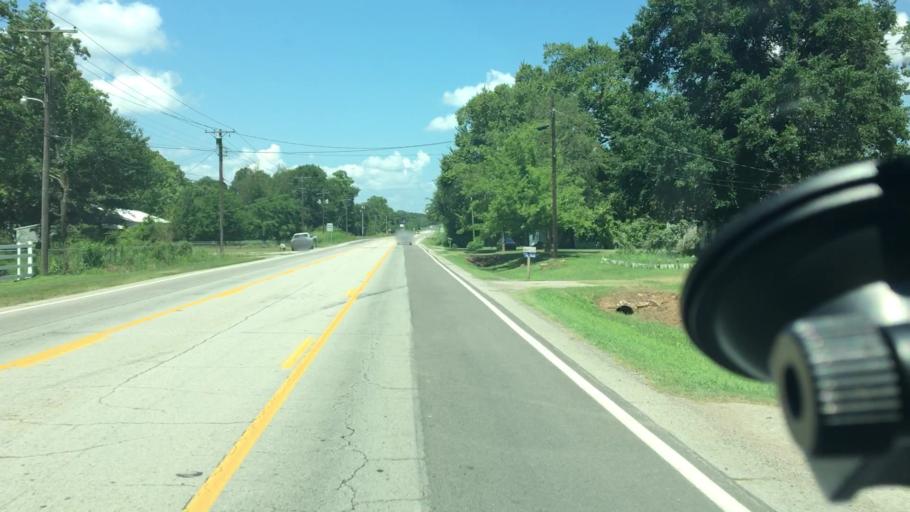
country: US
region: Arkansas
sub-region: Sebastian County
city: Lavaca
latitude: 35.2944
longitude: -94.1410
